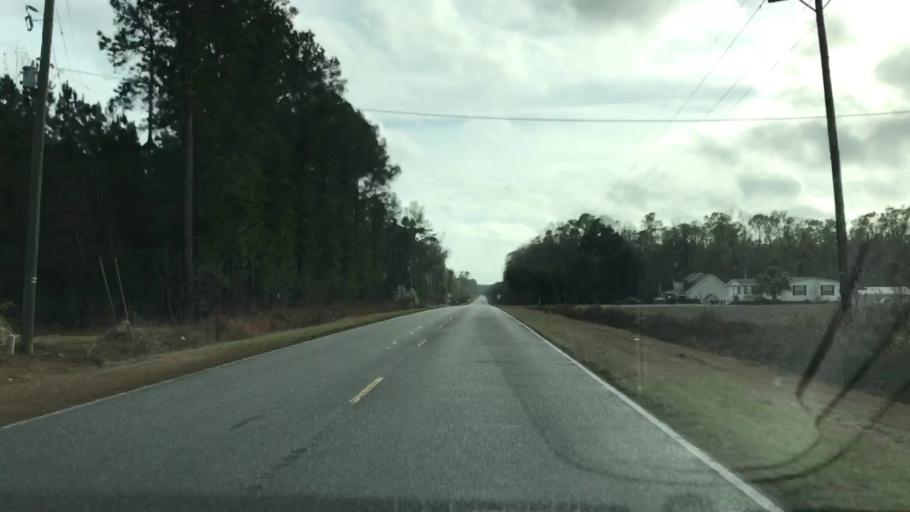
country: US
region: South Carolina
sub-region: Williamsburg County
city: Andrews
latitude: 33.4368
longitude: -79.5923
